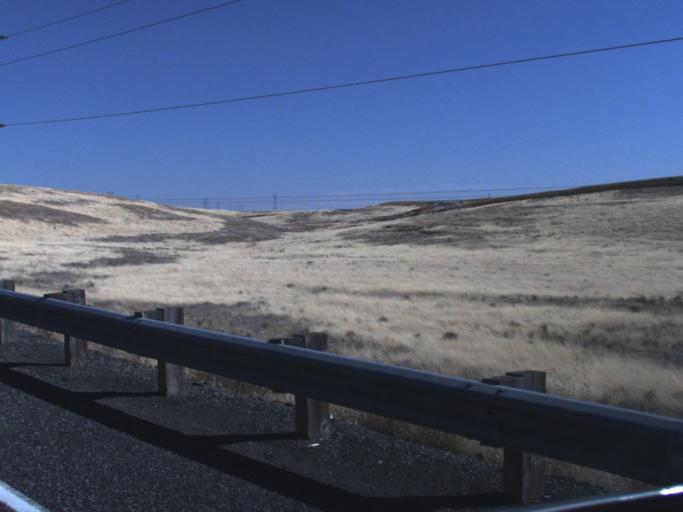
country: US
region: Washington
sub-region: Walla Walla County
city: Burbank
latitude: 46.2664
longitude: -118.7799
